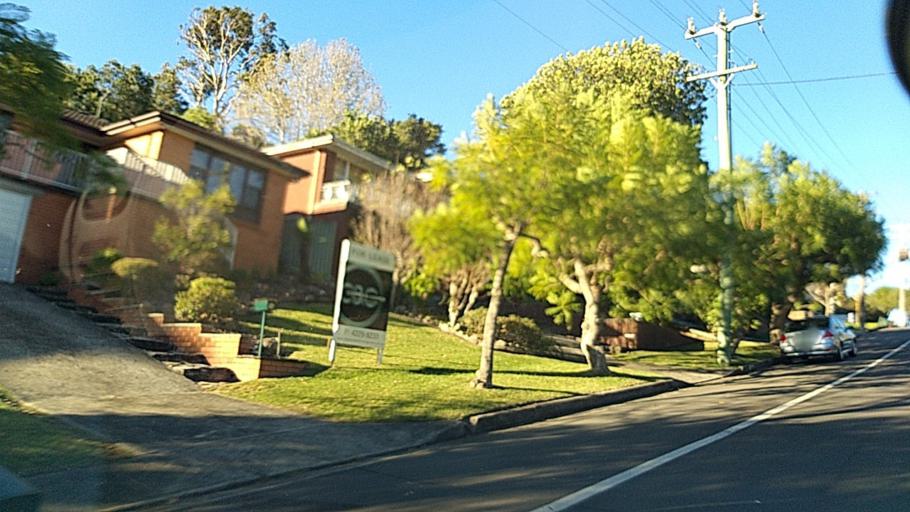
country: AU
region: New South Wales
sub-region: Wollongong
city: Mount Keira
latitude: -34.4241
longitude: 150.8490
